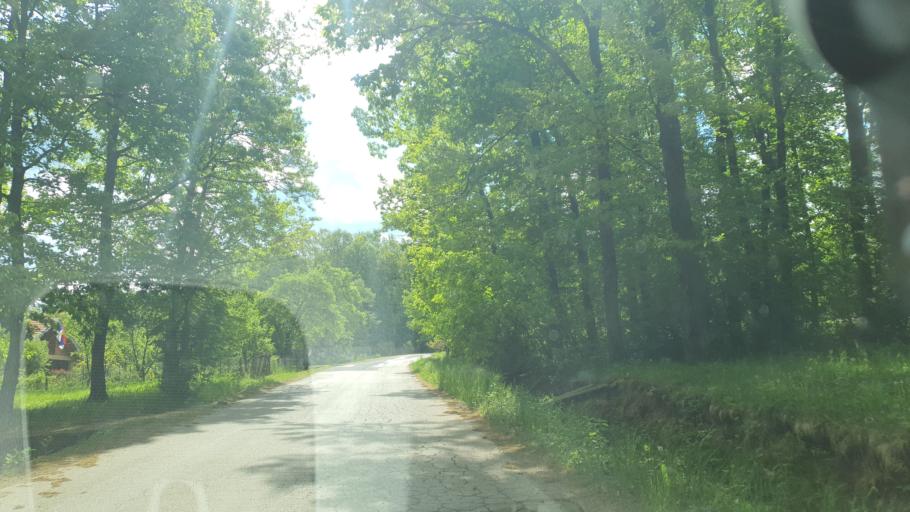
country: RS
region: Central Serbia
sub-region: Pomoravski Okrug
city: Paracin
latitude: 43.9496
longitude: 21.4885
